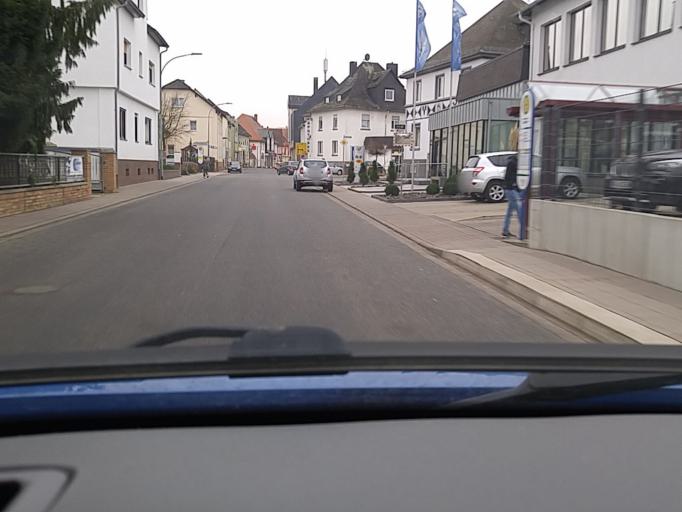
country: DE
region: Hesse
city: Reichelsheim
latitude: 50.3596
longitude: 8.8758
